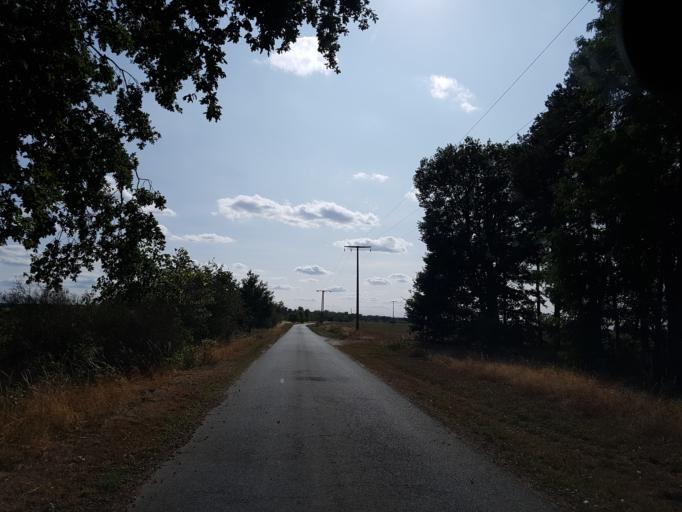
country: DE
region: Saxony-Anhalt
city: Seyda
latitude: 51.9543
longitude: 12.8766
